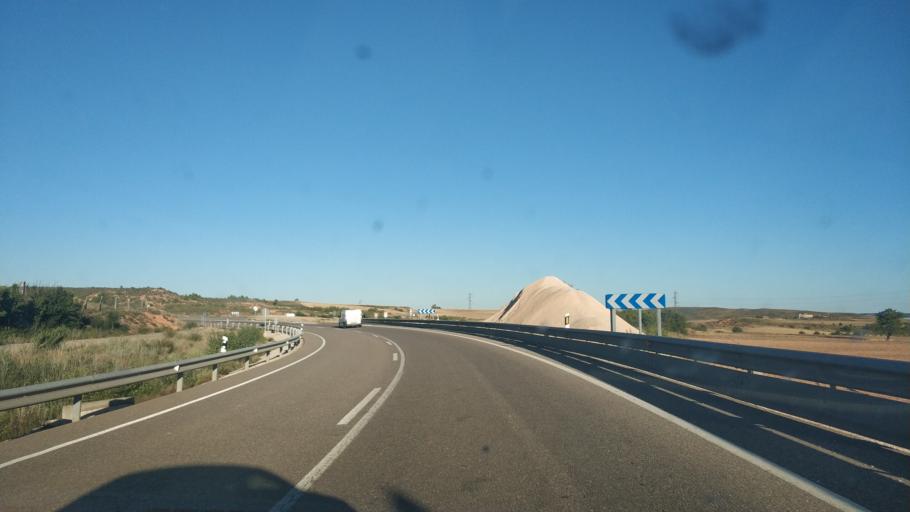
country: ES
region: Castille and Leon
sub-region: Provincia de Soria
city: San Esteban de Gormaz
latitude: 41.5657
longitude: -3.1859
